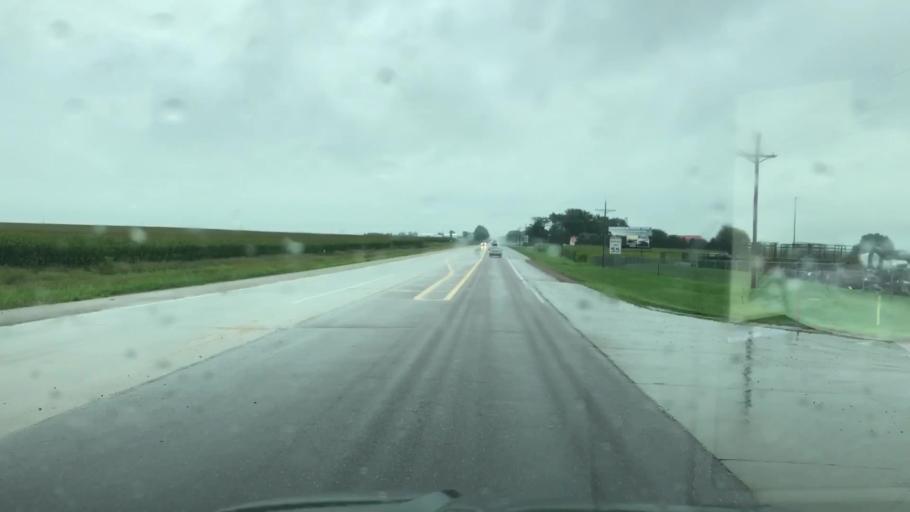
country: US
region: Iowa
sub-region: O'Brien County
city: Sheldon
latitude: 43.1861
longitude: -95.8092
